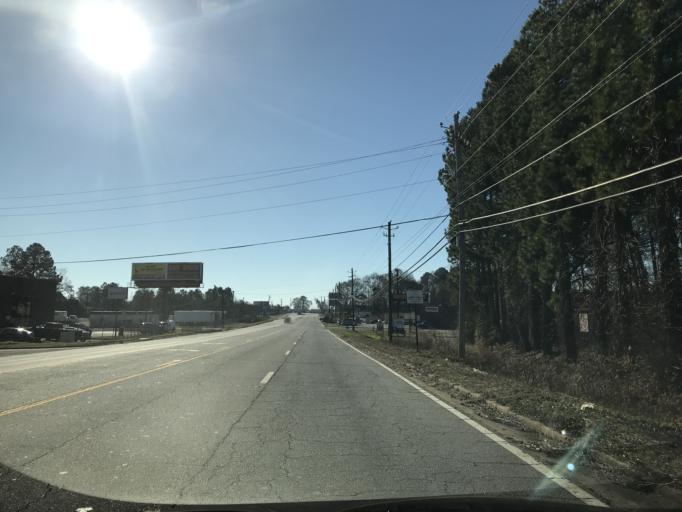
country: US
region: Georgia
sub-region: Fulton County
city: Hapeville
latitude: 33.6268
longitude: -84.4096
